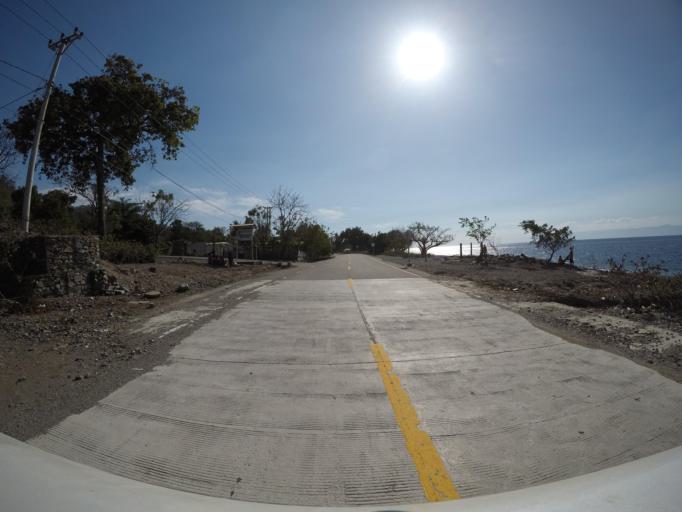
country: TL
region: Liquica
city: Maubara
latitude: -8.6189
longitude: 125.1760
